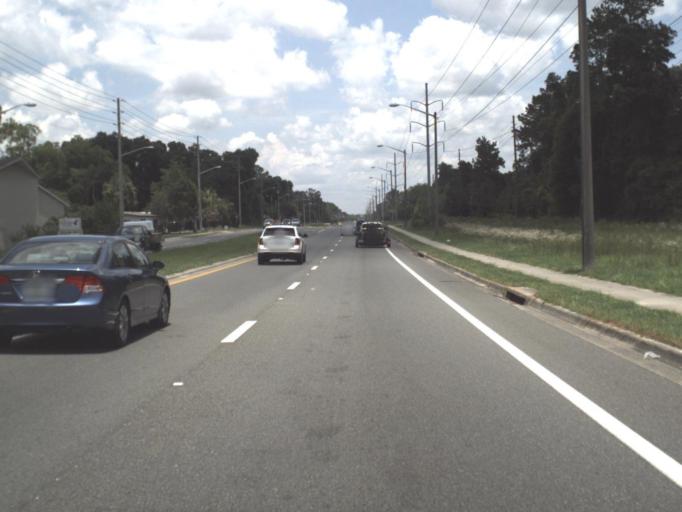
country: US
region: Florida
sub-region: Alachua County
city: Gainesville
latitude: 29.6063
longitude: -82.4071
